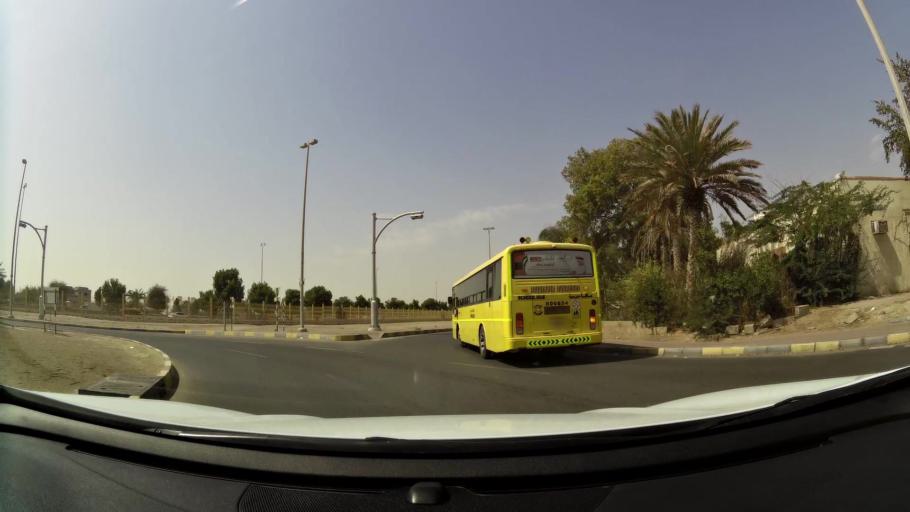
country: AE
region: Abu Dhabi
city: Abu Dhabi
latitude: 24.2893
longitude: 54.6384
